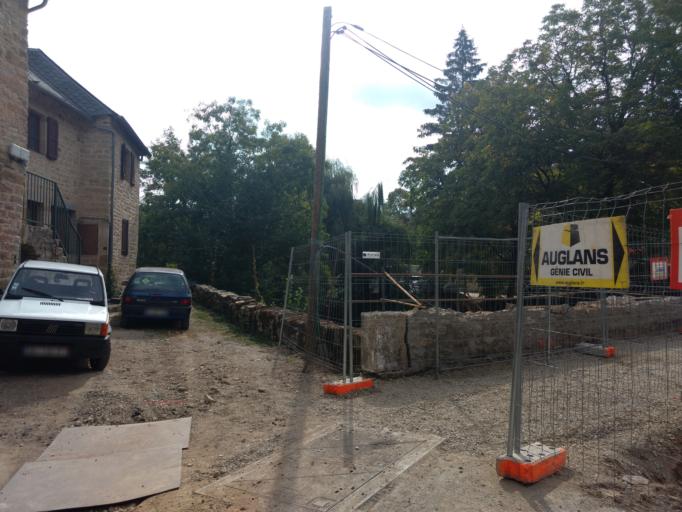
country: FR
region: Midi-Pyrenees
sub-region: Departement de l'Aveyron
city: Bozouls
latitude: 44.4680
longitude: 2.7167
